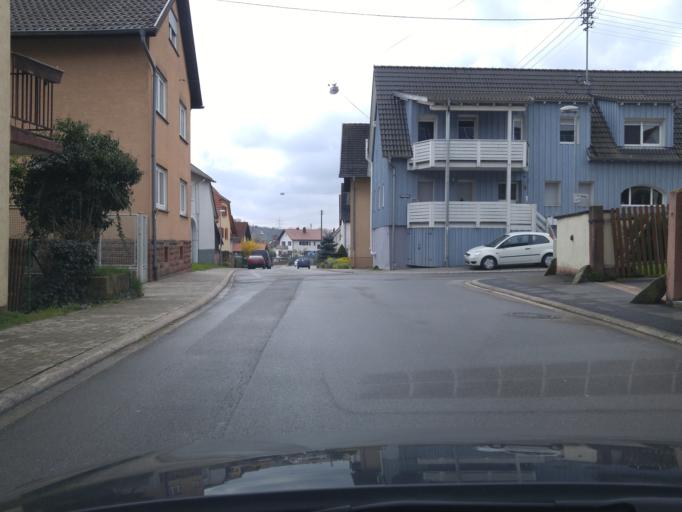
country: DE
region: Baden-Wuerttemberg
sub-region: Karlsruhe Region
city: Neckarbischofsheim
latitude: 49.3242
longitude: 8.9727
